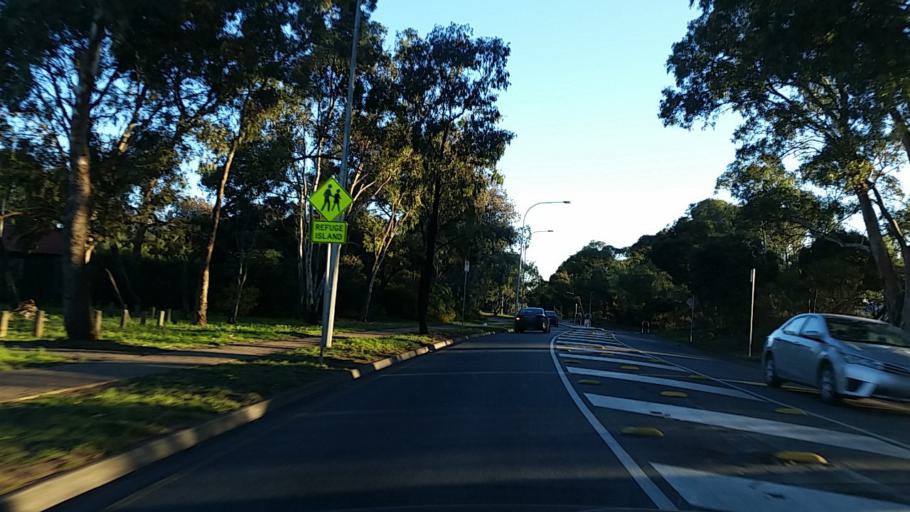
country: AU
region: South Australia
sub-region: Salisbury
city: Salisbury
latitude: -34.7776
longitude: 138.6122
